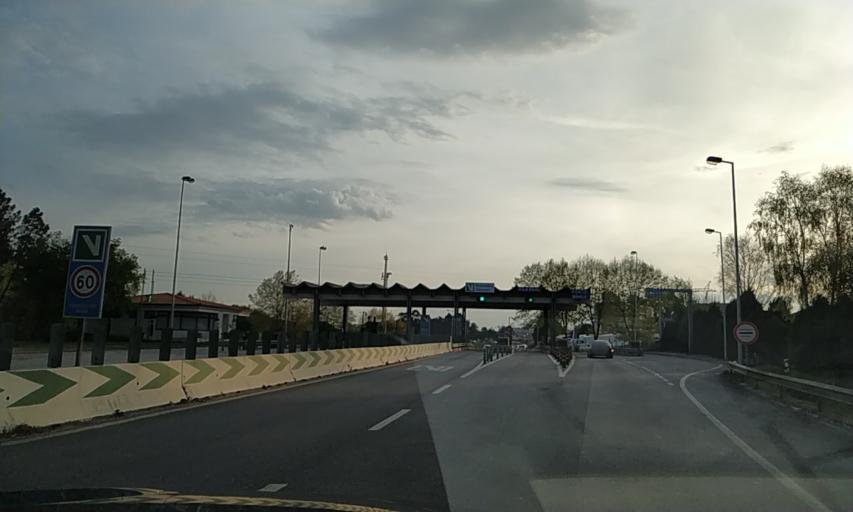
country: PT
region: Porto
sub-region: Gondomar
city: Baguim do Monte
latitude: 41.2035
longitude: -8.5503
